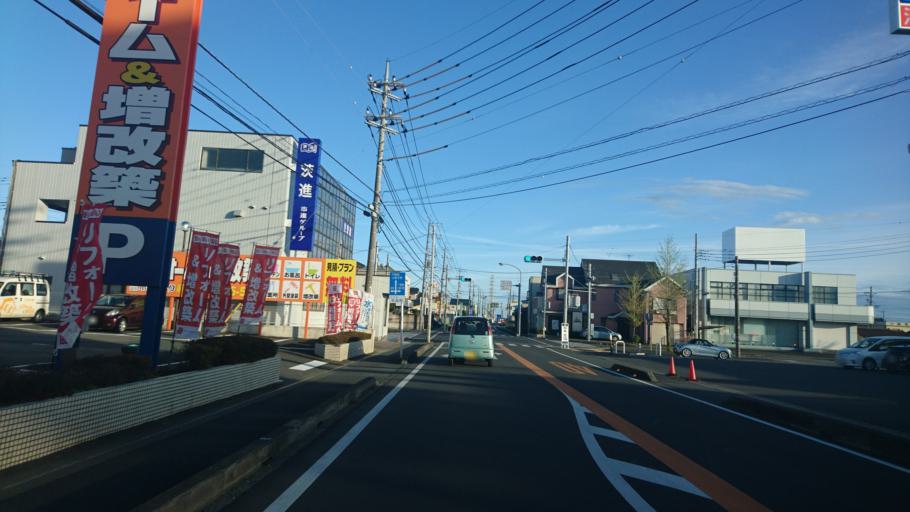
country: JP
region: Ibaraki
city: Ishige
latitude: 36.1837
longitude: 139.9674
